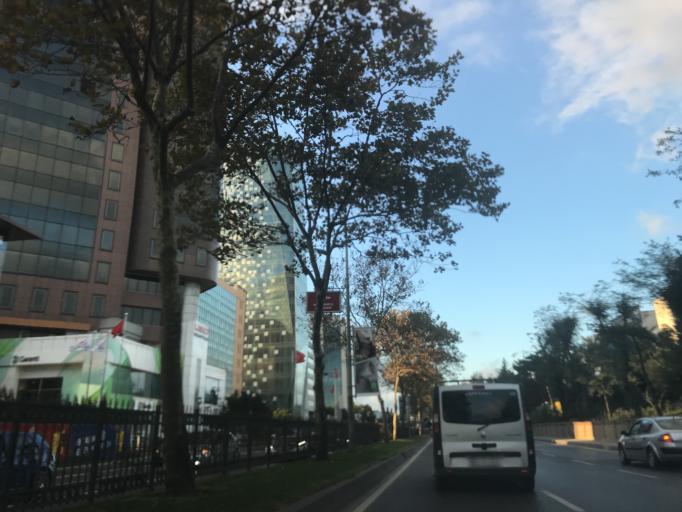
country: TR
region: Istanbul
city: Sisli
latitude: 41.1109
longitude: 29.0252
